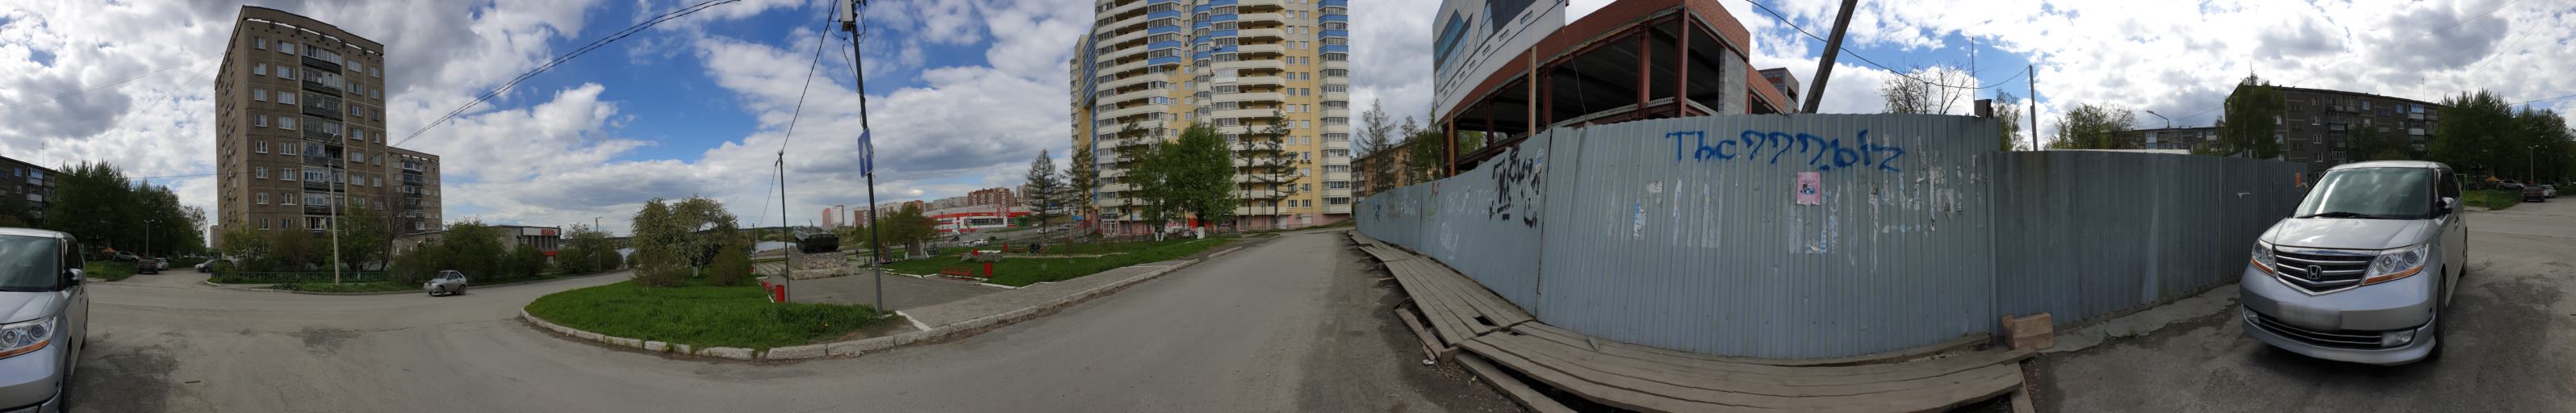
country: RU
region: Sverdlovsk
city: Pervoural'sk
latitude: 56.9133
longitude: 59.9439
